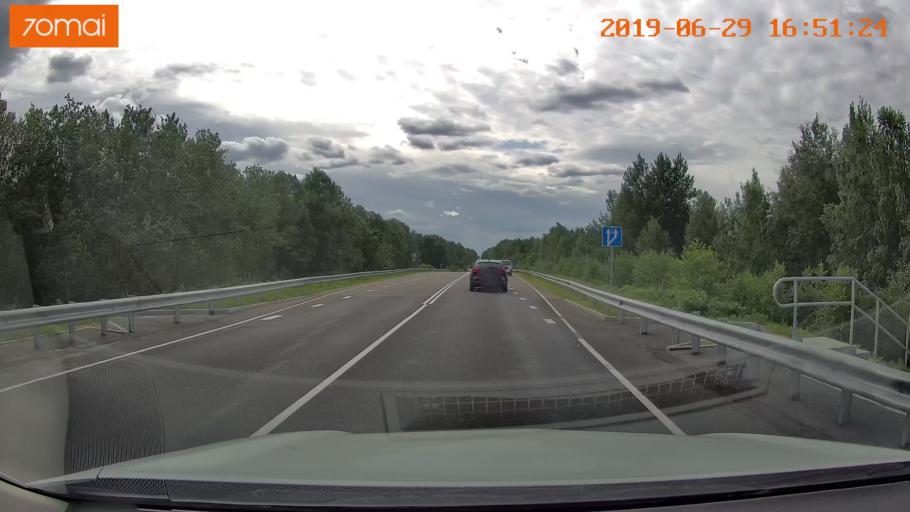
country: BY
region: Brest
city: Luninyets
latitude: 52.2808
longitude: 26.8255
